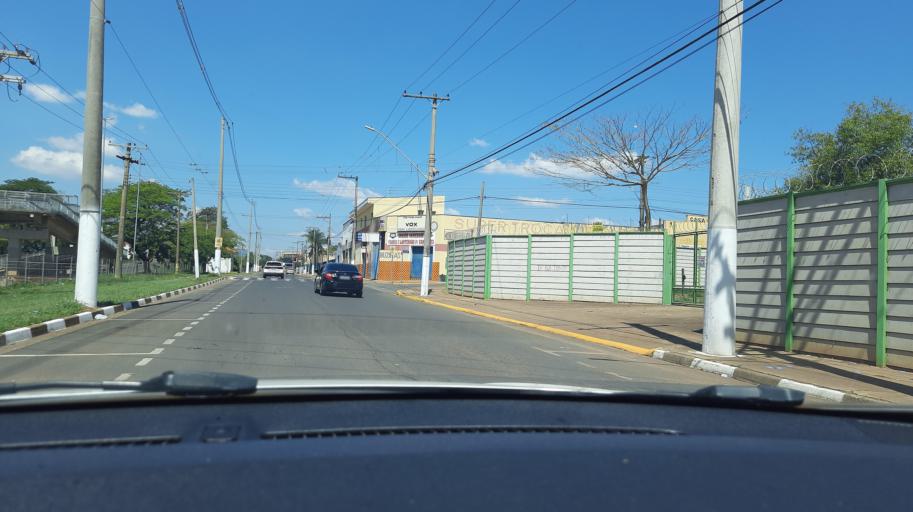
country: BR
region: Sao Paulo
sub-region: Vargem Grande Do Sul
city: Vargem Grande do Sul
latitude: -21.8421
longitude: -46.9055
